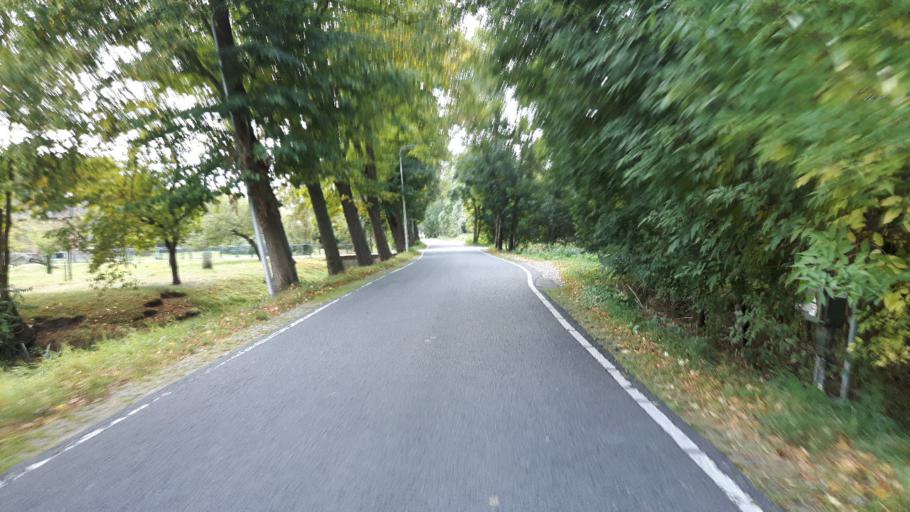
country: NL
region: South Holland
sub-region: Bodegraven-Reeuwijk
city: Bodegraven
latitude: 52.1019
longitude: 4.7533
